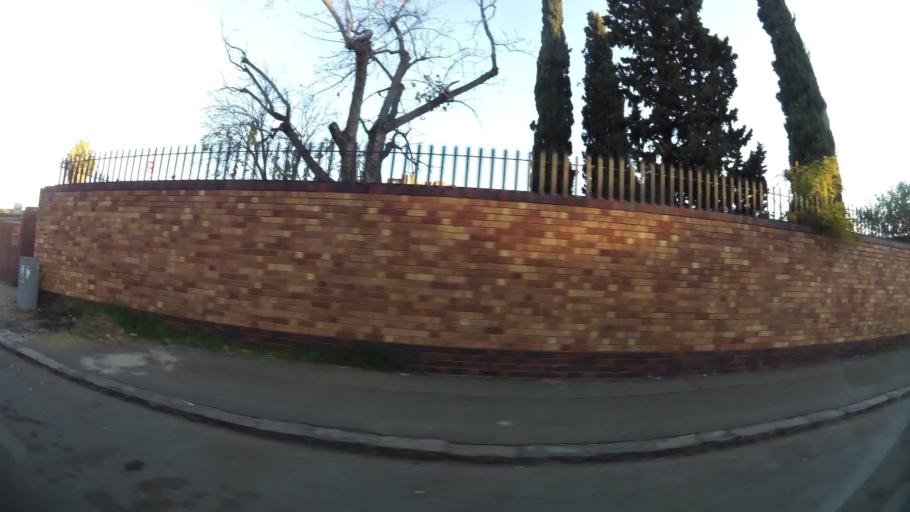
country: ZA
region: Northern Cape
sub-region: Frances Baard District Municipality
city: Kimberley
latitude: -28.7415
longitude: 24.7661
